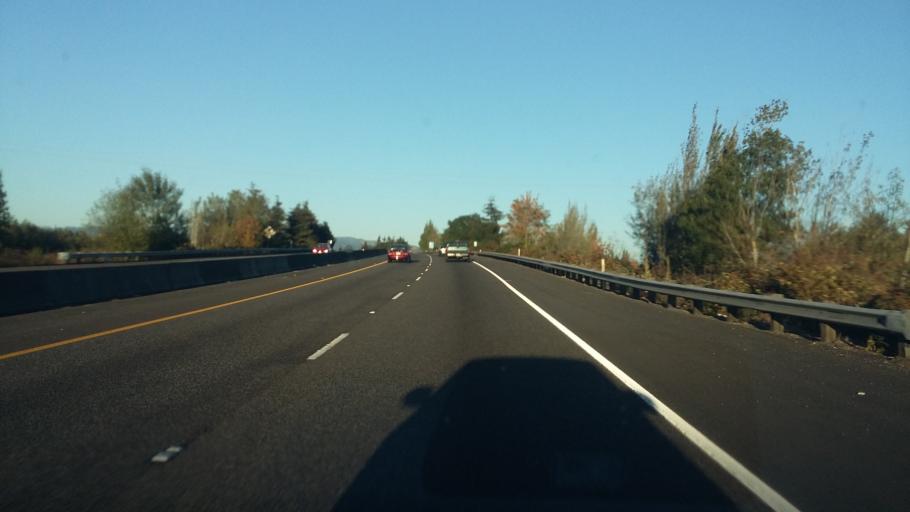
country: US
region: Washington
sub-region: Clark County
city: Walnut Grove
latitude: 45.6479
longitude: -122.6059
